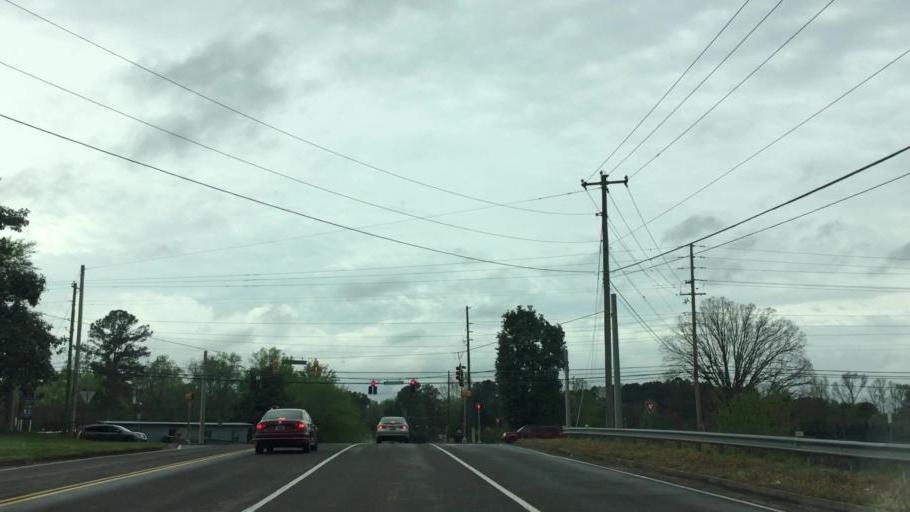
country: US
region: Georgia
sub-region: Cherokee County
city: Canton
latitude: 34.2117
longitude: -84.3962
